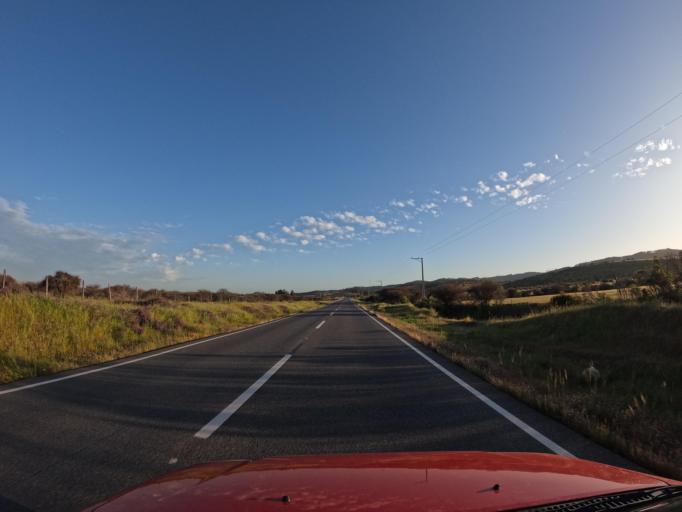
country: CL
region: O'Higgins
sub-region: Provincia de Colchagua
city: Santa Cruz
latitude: -34.3209
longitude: -71.7435
